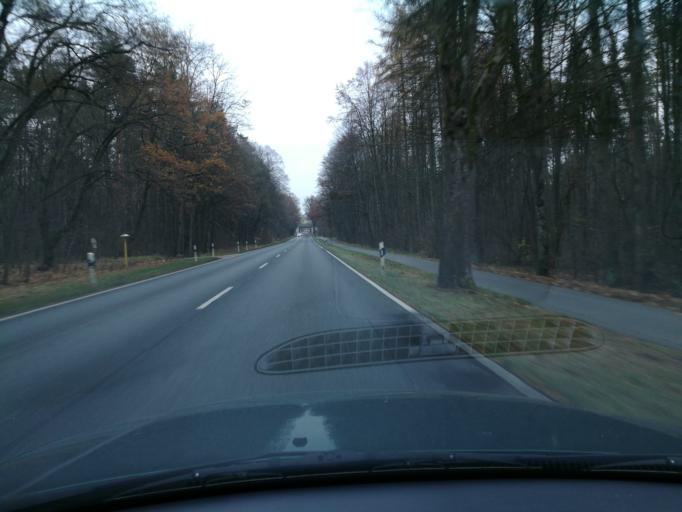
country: DE
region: Bavaria
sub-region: Regierungsbezirk Mittelfranken
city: Feucht
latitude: 49.3873
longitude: 11.1964
